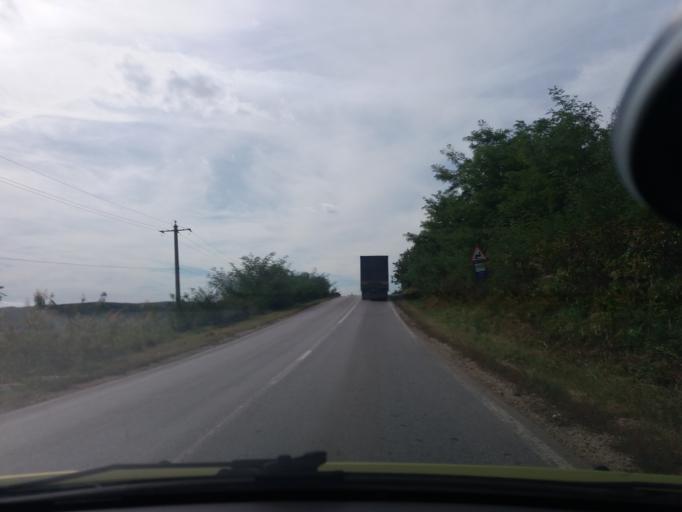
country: RO
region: Alba
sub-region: Municipiul Blaj
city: Izvoarele
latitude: 46.1742
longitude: 23.8915
